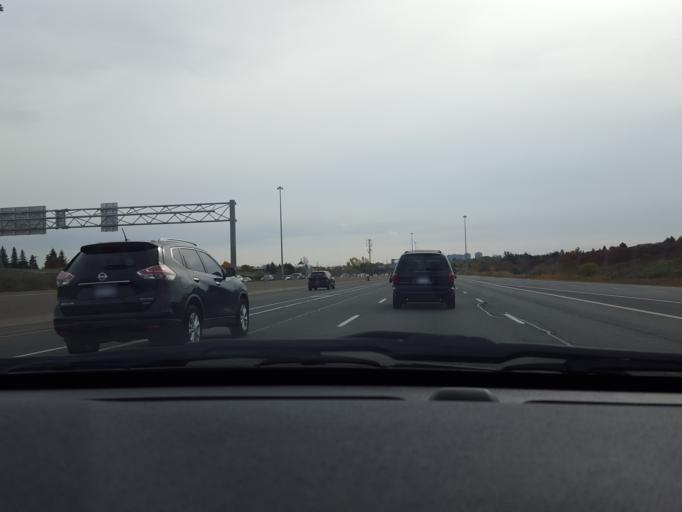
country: CA
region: Ontario
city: Willowdale
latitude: 43.8348
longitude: -79.3669
